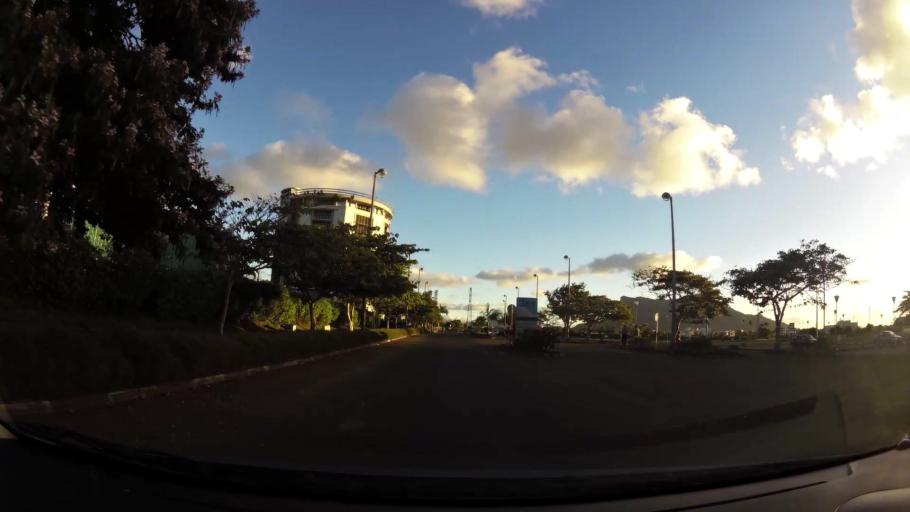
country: MU
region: Plaines Wilhems
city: Ebene
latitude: -20.2464
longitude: 57.4923
